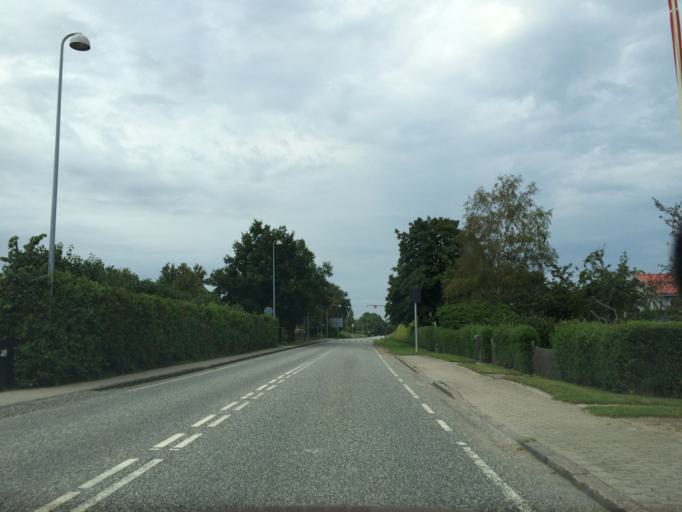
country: DK
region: South Denmark
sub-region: Sonderborg Kommune
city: Broager
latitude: 54.9200
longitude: 9.6824
